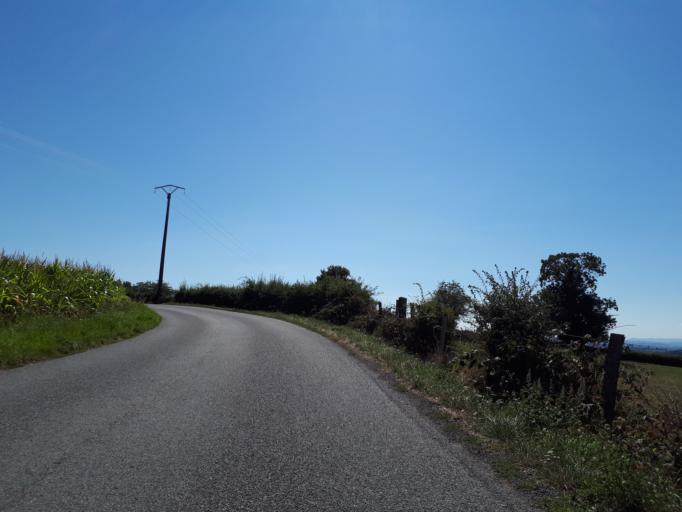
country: FR
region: Rhone-Alpes
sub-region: Departement de la Loire
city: Bussieres
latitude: 45.8296
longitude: 4.2888
